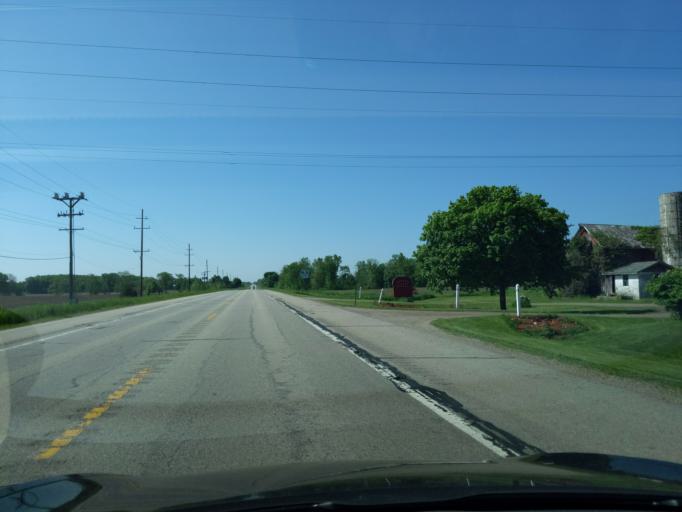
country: US
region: Michigan
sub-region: Ingham County
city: Webberville
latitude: 42.5694
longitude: -84.1922
